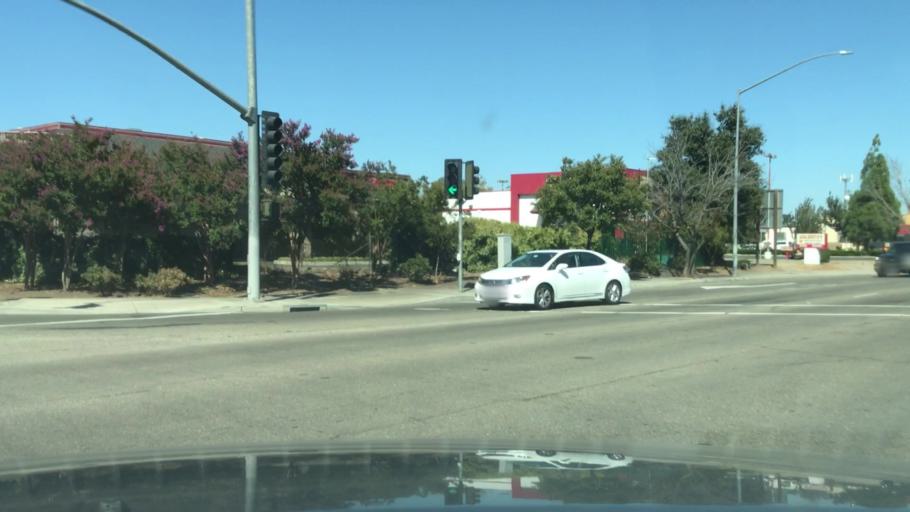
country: US
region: California
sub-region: San Joaquin County
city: Lincoln Village
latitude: 38.0212
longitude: -121.3582
